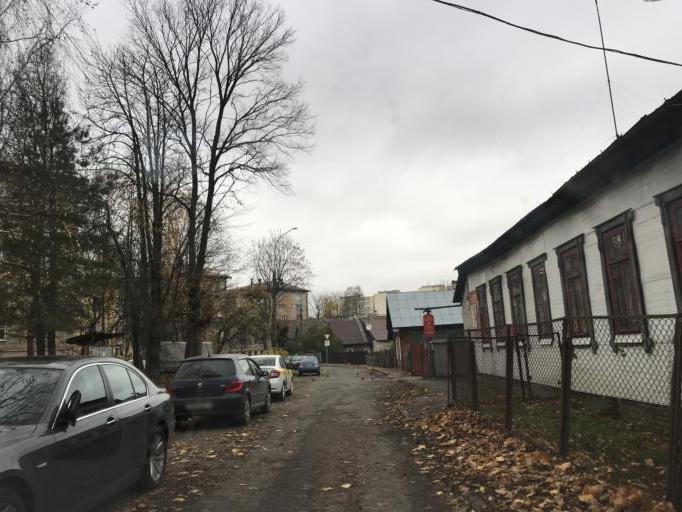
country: BY
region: Mogilev
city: Mahilyow
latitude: 53.9018
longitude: 30.3466
